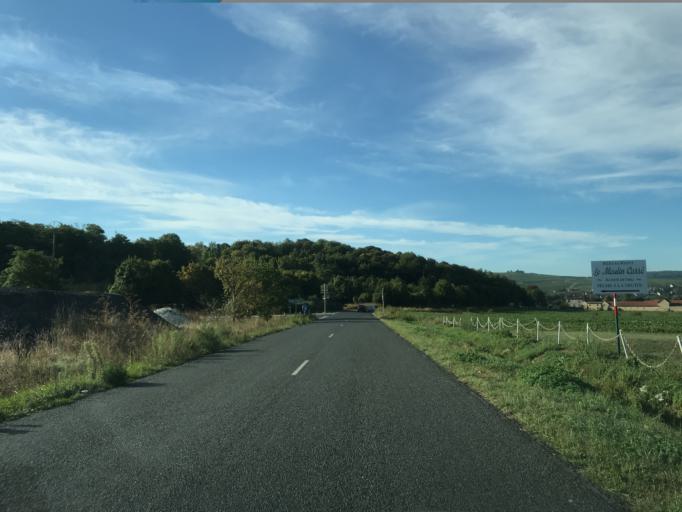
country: FR
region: Champagne-Ardenne
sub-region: Departement de la Marne
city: Chatillon-sur-Marne
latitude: 49.0960
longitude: 3.7672
